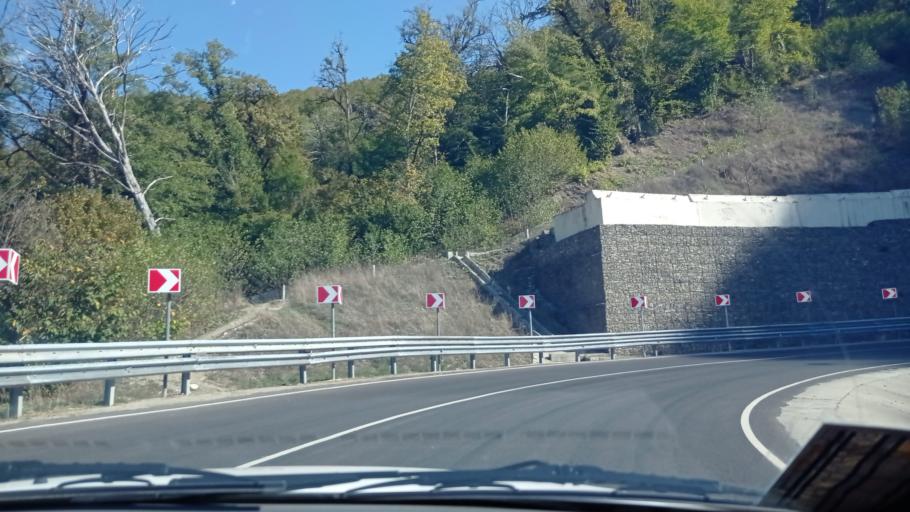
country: RU
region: Krasnodarskiy
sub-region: Sochi City
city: Krasnaya Polyana
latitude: 43.6821
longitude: 40.2458
